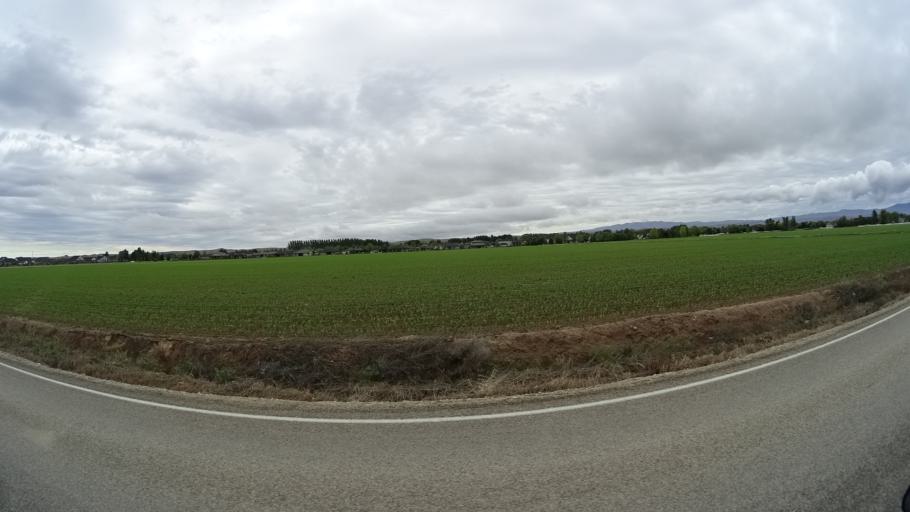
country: US
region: Idaho
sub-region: Ada County
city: Eagle
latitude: 43.7060
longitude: -116.4102
